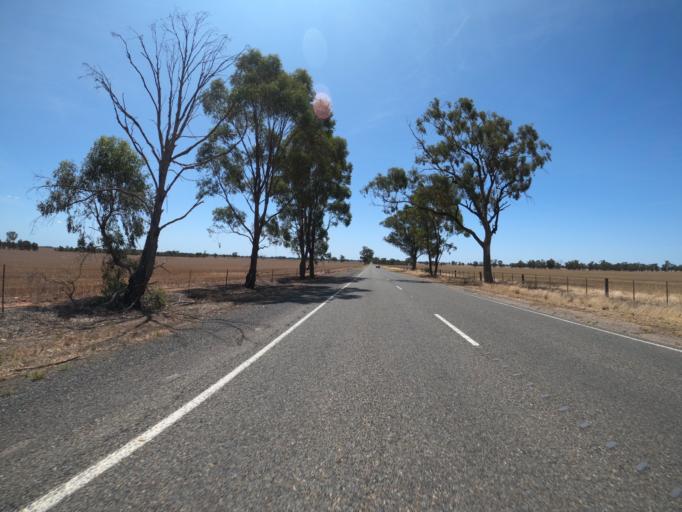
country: AU
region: Victoria
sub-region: Moira
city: Yarrawonga
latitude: -36.0772
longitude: 145.9954
